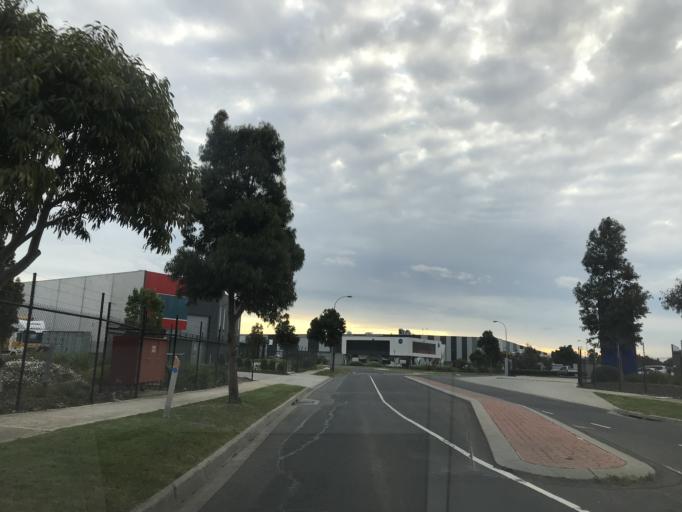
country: AU
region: Victoria
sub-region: Brimbank
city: Derrimut
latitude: -37.8047
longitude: 144.7686
